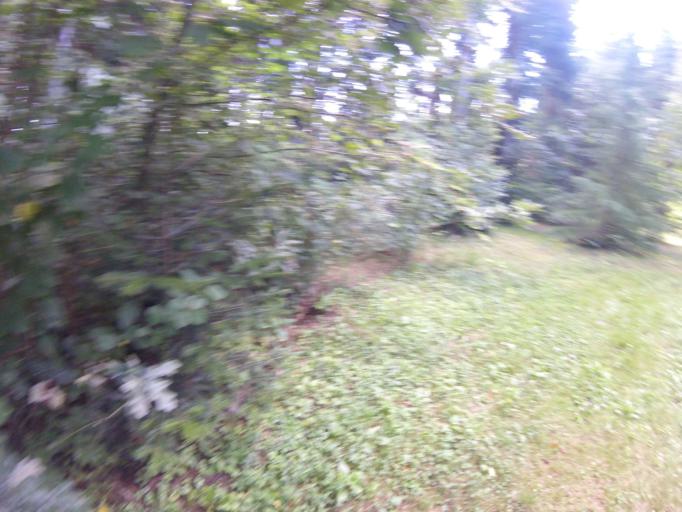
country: HU
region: Zala
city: Letenye
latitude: 46.5066
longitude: 16.7006
